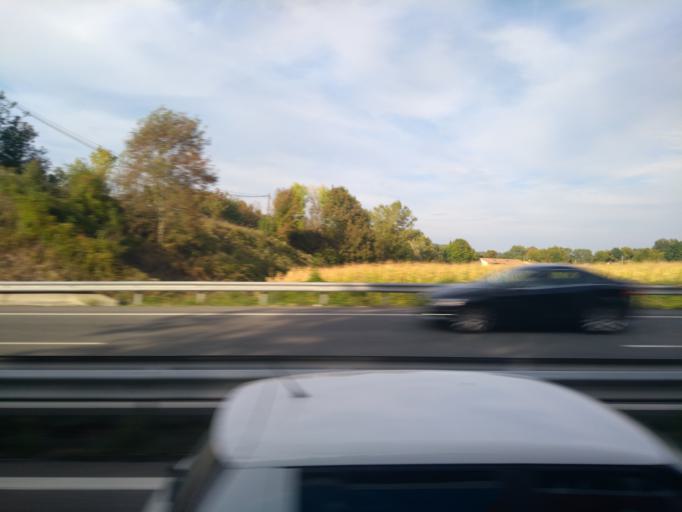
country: FR
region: Rhone-Alpes
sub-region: Departement de l'Isere
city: Cessieu
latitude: 45.5490
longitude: 5.3710
